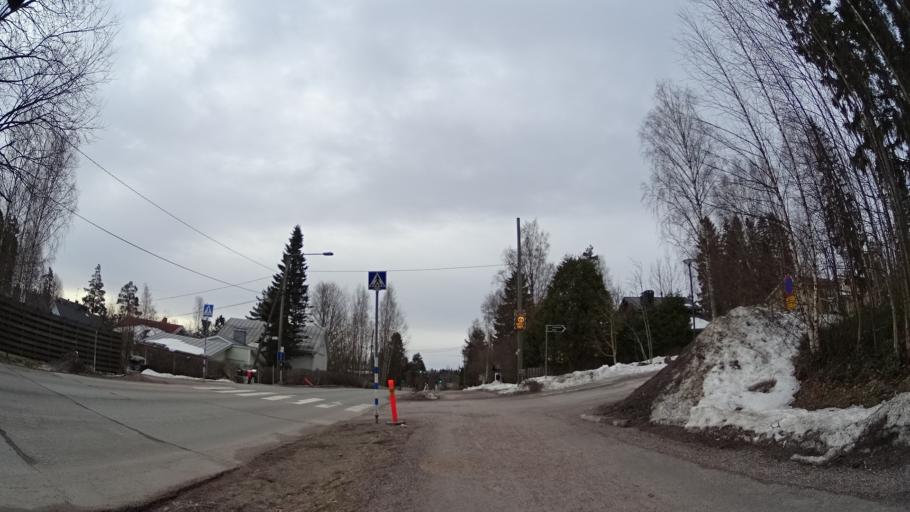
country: FI
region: Uusimaa
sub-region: Helsinki
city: Kilo
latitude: 60.2389
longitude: 24.8087
